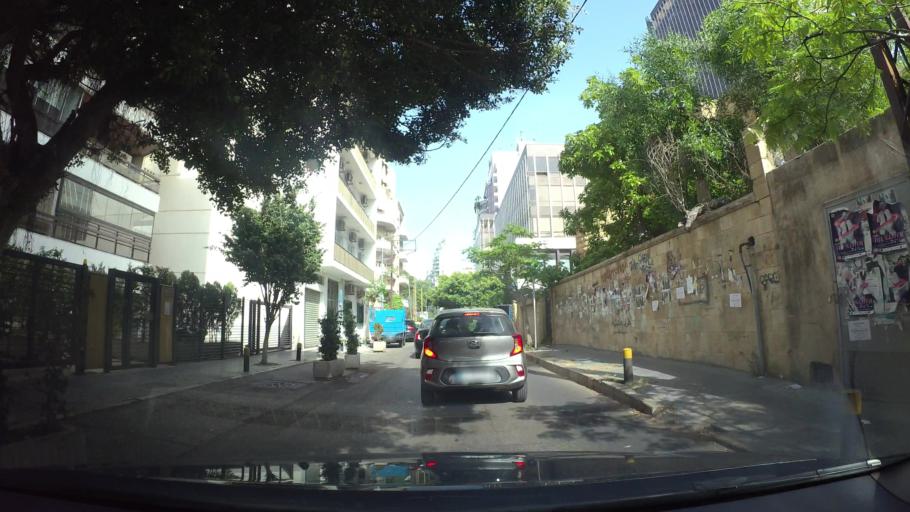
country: LB
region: Beyrouth
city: Ra's Bayrut
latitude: 33.8986
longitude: 35.4864
